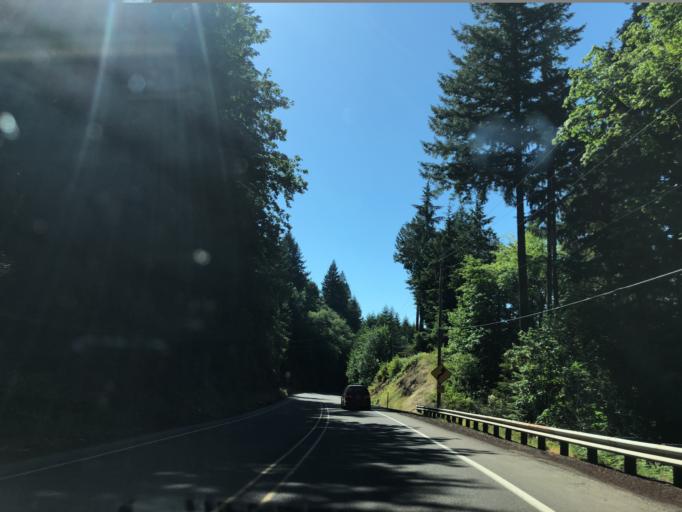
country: US
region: Oregon
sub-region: Linn County
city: Sweet Home
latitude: 44.4124
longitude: -122.6146
